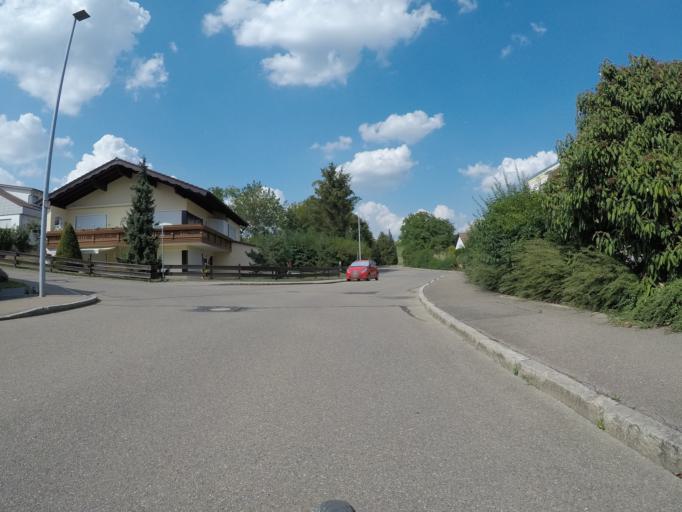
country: DE
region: Baden-Wuerttemberg
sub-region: Tuebingen Region
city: Eningen unter Achalm
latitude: 48.4938
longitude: 9.2564
